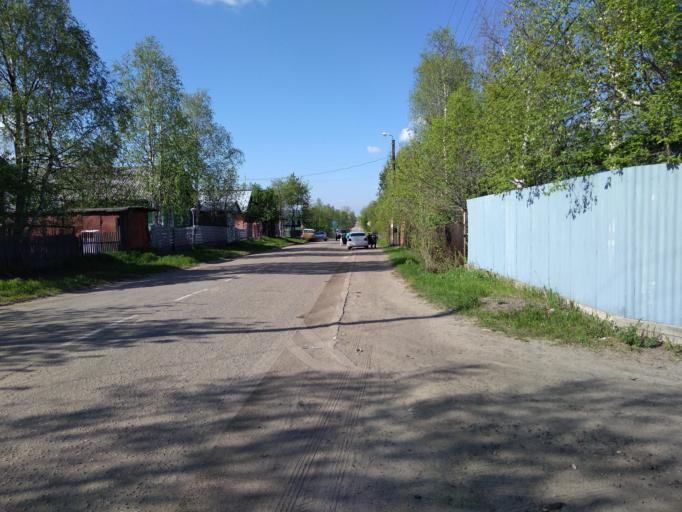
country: RU
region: Komi Republic
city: Puteyets
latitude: 65.1146
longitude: 57.1480
